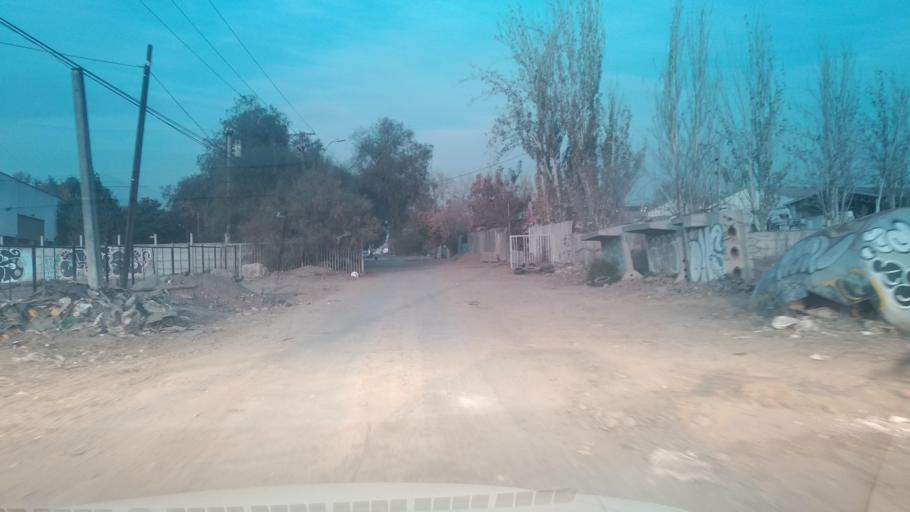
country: CL
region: Santiago Metropolitan
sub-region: Provincia de Chacabuco
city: Chicureo Abajo
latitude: -33.3465
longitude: -70.7183
